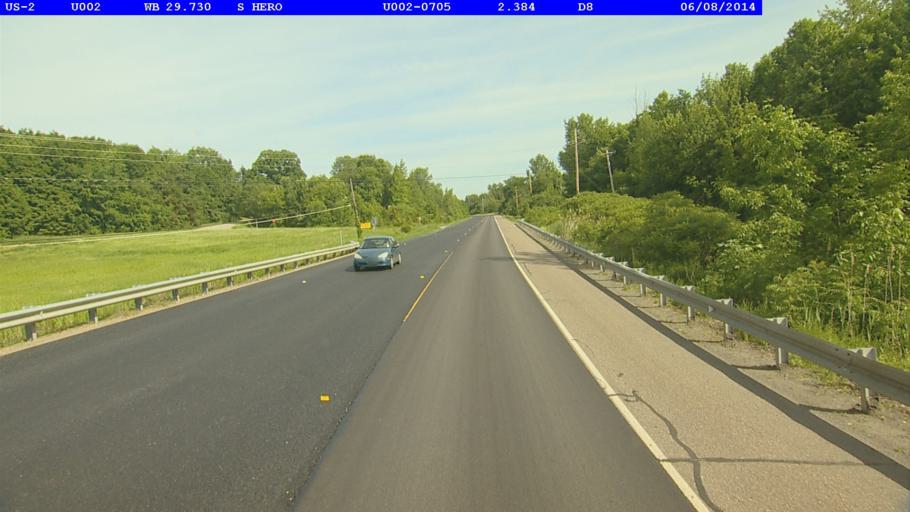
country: US
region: New York
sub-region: Clinton County
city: Cumberland Head
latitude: 44.6478
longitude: -73.3152
